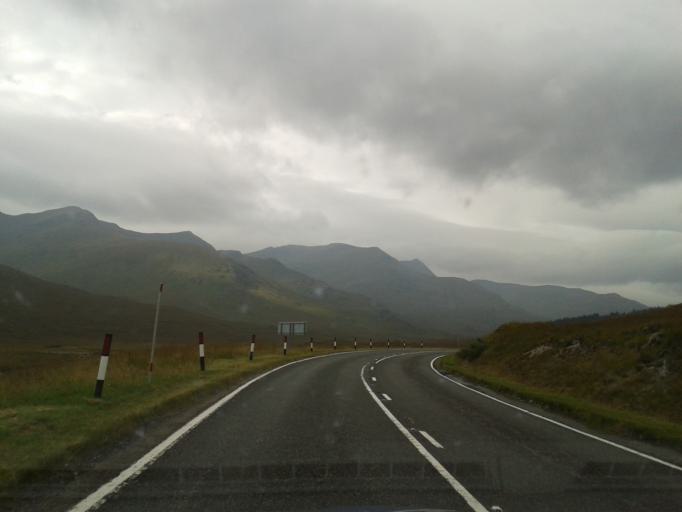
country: GB
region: Scotland
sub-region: Highland
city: Fort William
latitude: 57.1532
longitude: -5.1976
